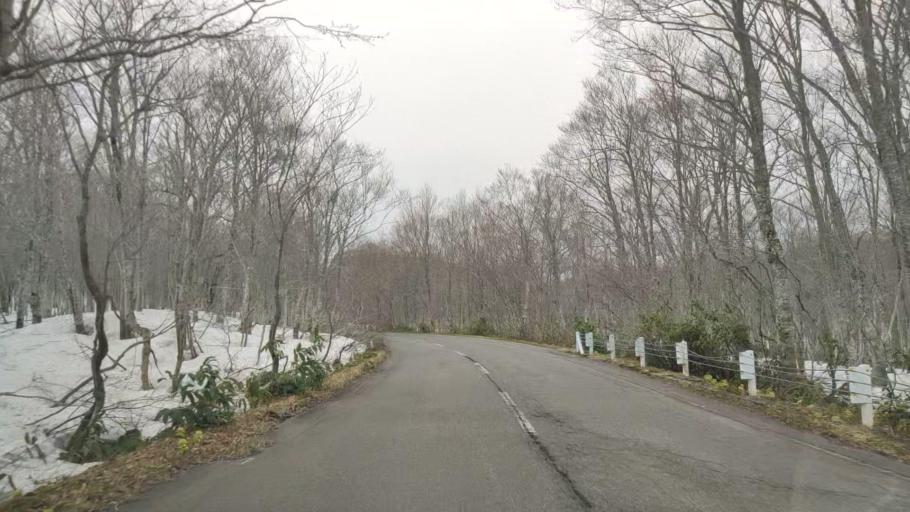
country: JP
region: Aomori
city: Aomori Shi
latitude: 40.6504
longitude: 140.9462
